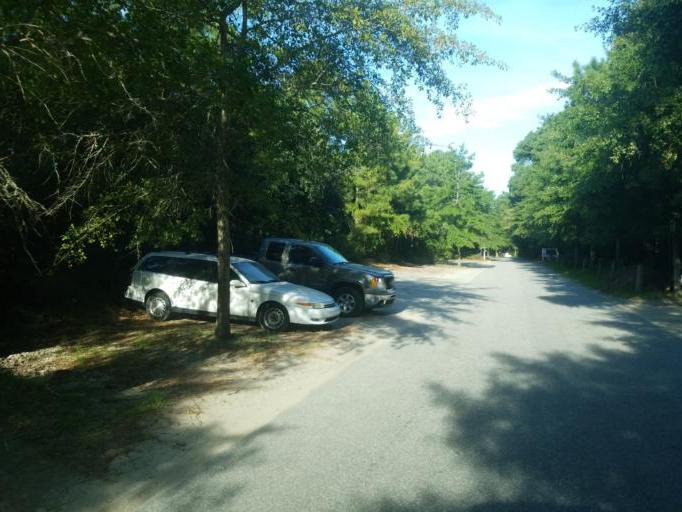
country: US
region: North Carolina
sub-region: Currituck County
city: Currituck
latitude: 36.3761
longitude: -75.8298
